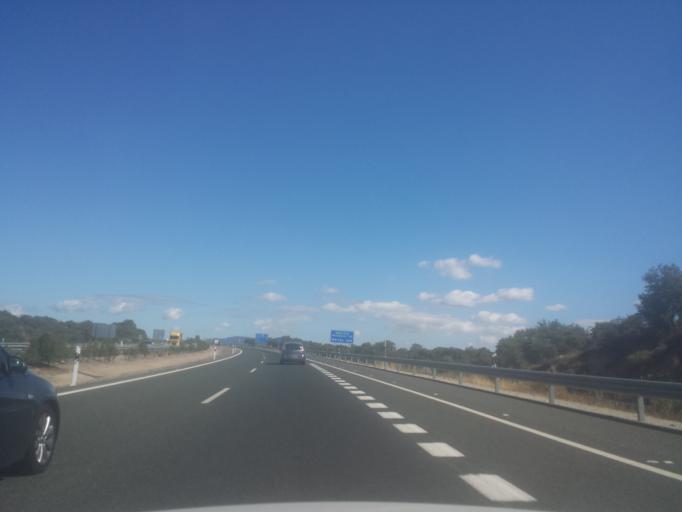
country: ES
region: Andalusia
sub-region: Provincia de Huelva
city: Santa Olalla del Cala
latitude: 37.9078
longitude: -6.2139
